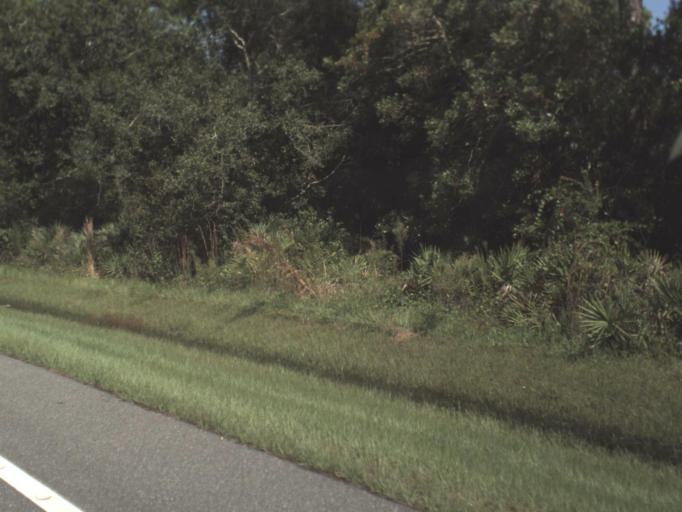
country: US
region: Florida
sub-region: Sarasota County
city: Lake Sarasota
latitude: 27.2586
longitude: -82.4023
